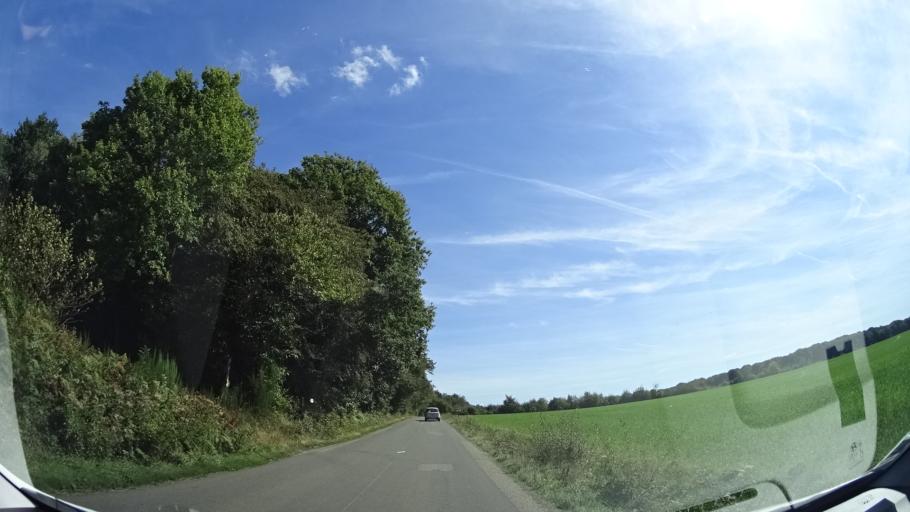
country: FR
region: Brittany
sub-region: Departement d'Ille-et-Vilaine
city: Saint-Sulpice-la-Foret
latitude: 48.2163
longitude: -1.5609
